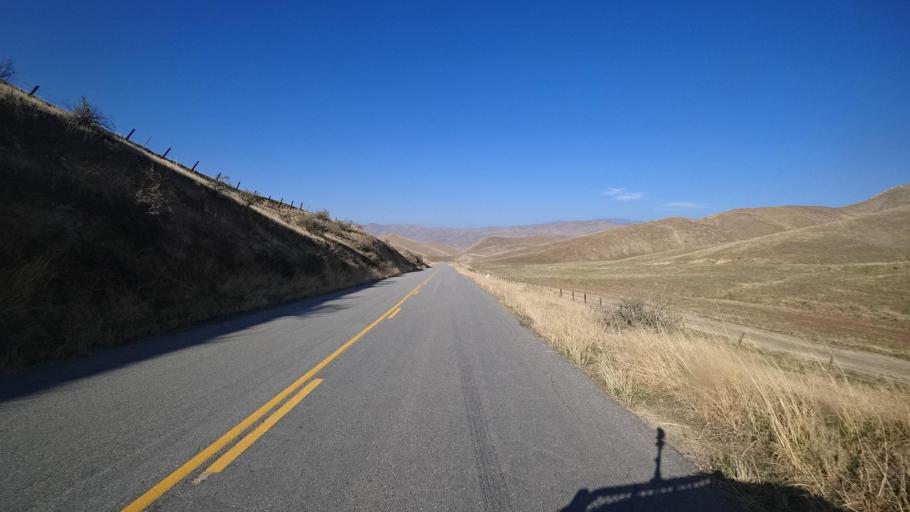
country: US
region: California
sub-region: Kern County
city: Bear Valley Springs
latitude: 35.2846
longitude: -118.6951
